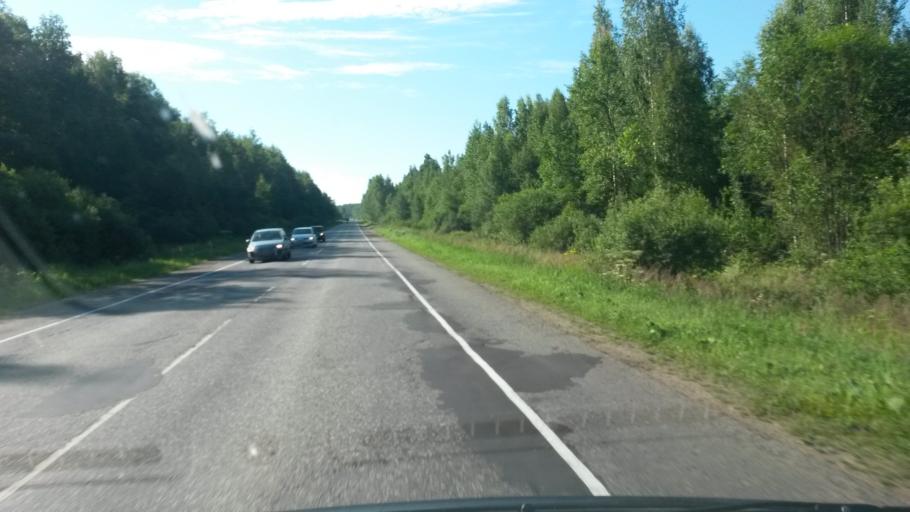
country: RU
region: Ivanovo
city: Pistsovo
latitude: 57.1025
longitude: 40.6536
